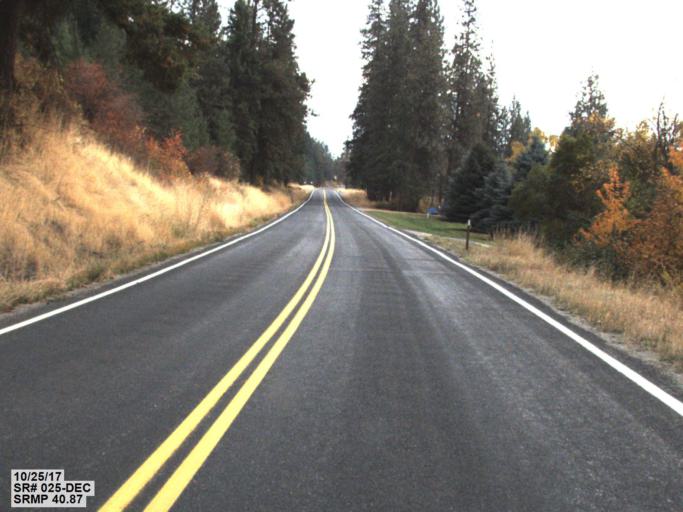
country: US
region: Washington
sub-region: Lincoln County
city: Davenport
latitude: 48.1090
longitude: -118.2040
